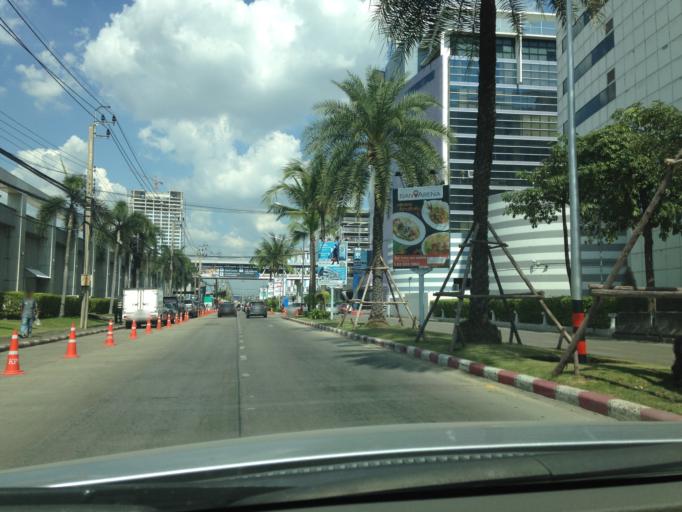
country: TH
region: Bangkok
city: Lak Si
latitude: 13.9105
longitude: 100.5491
